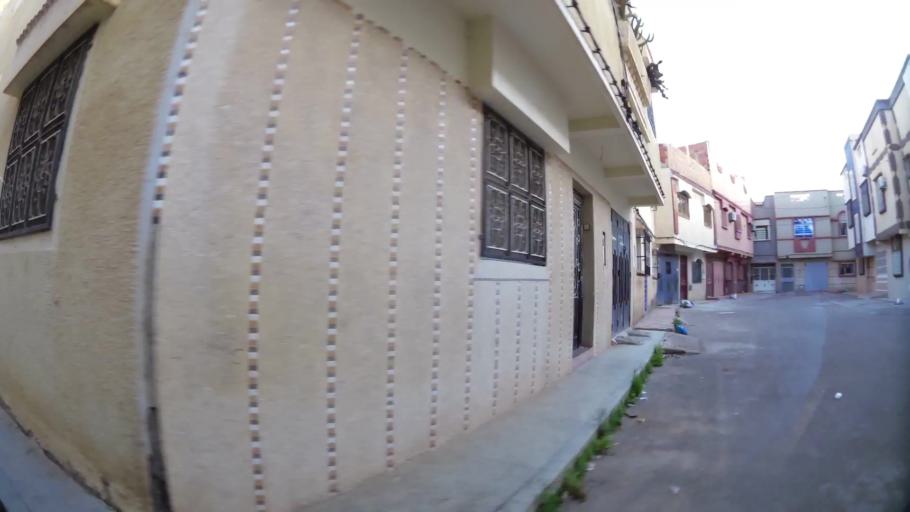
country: MA
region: Oriental
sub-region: Oujda-Angad
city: Oujda
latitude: 34.6762
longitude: -1.8928
